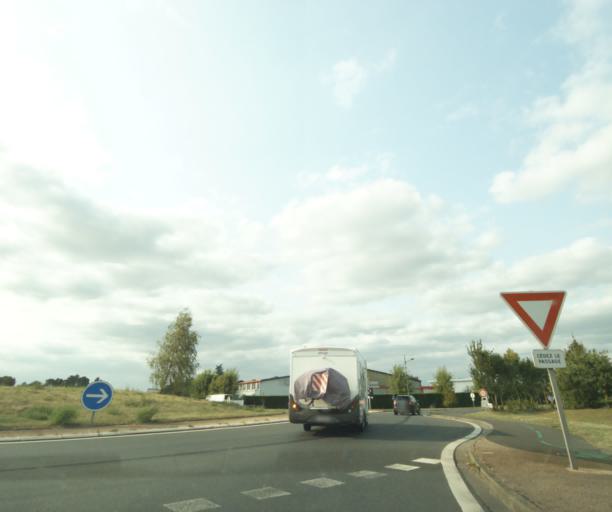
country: FR
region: Centre
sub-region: Departement d'Indre-et-Loire
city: Esvres
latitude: 47.2983
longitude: 0.8003
